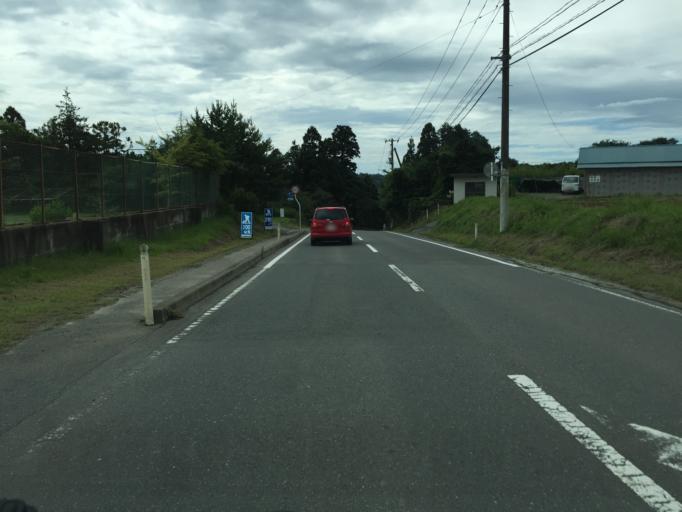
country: JP
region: Miyagi
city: Marumori
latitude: 37.7598
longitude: 140.9918
